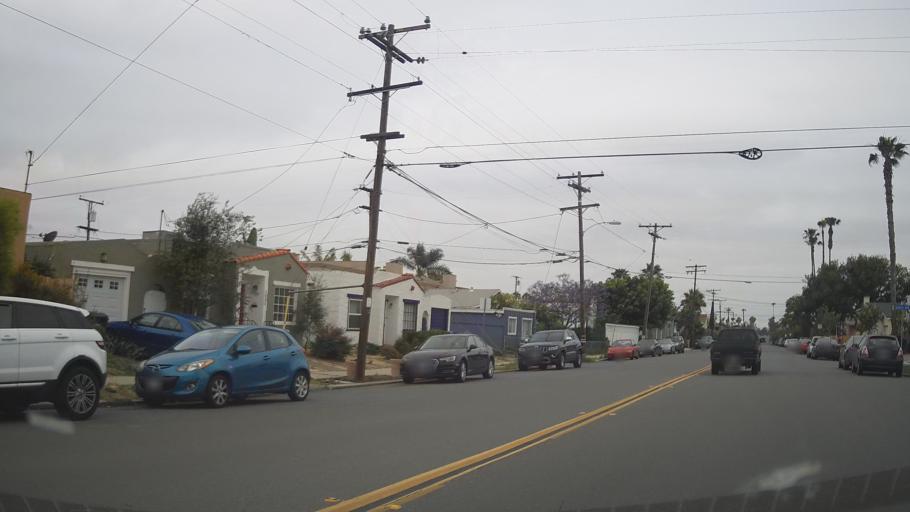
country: US
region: California
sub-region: San Diego County
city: San Diego
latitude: 32.7591
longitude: -117.1387
